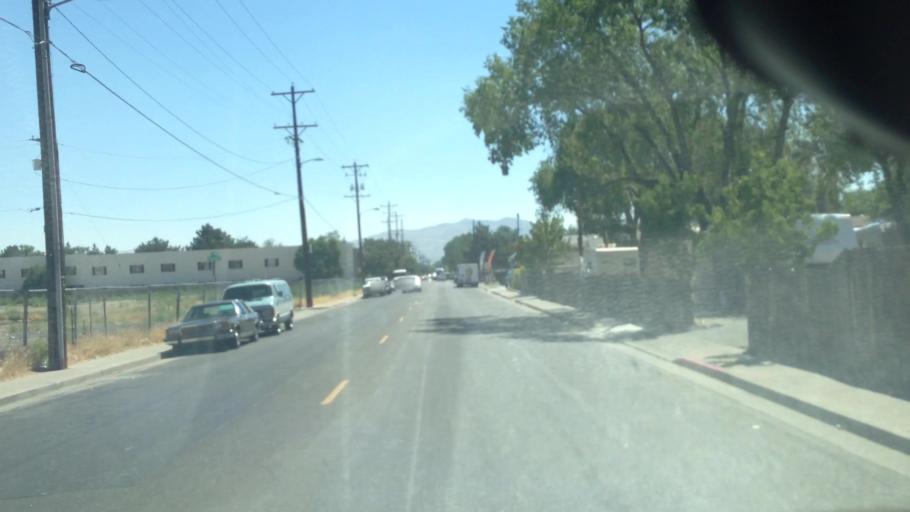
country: US
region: Nevada
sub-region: Washoe County
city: Reno
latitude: 39.5009
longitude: -119.7989
